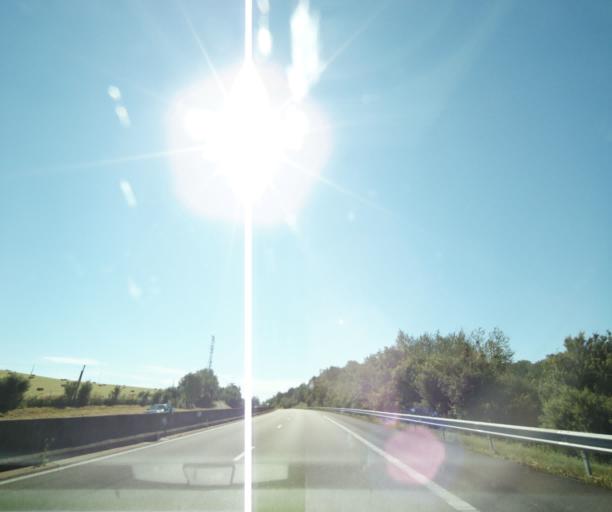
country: FR
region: Champagne-Ardenne
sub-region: Departement de la Haute-Marne
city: Nogent-le-Bas
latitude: 47.9533
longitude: 5.4228
